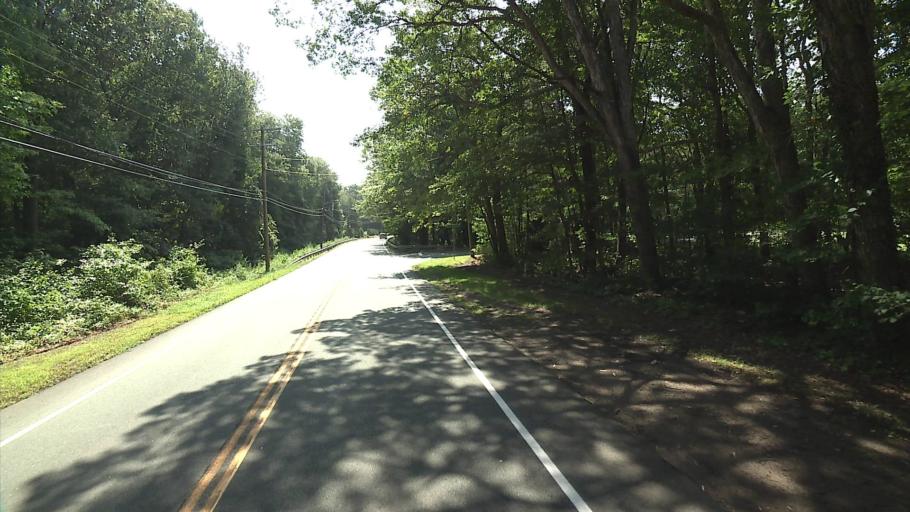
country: US
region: Connecticut
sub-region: New Haven County
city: Madison Center
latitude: 41.3155
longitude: -72.6067
